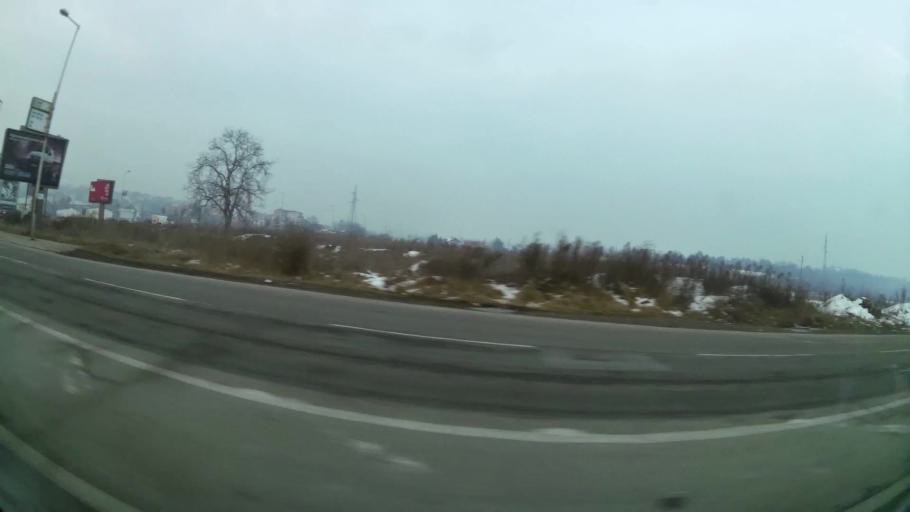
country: MK
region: Suto Orizari
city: Suto Orizare
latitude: 42.0246
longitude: 21.4090
